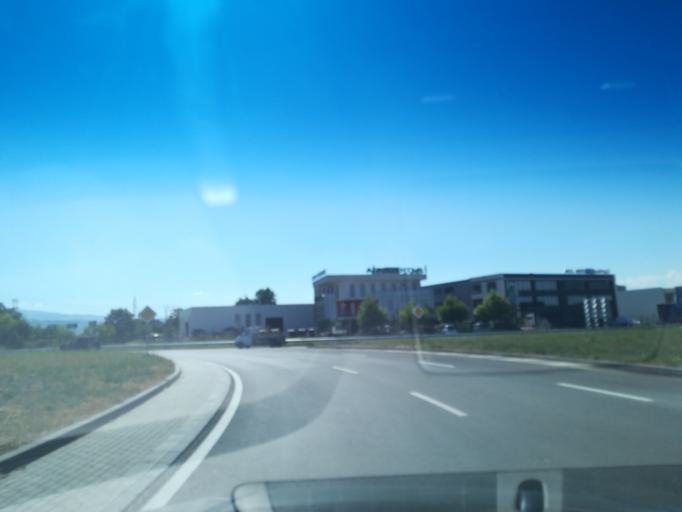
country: BG
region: Plovdiv
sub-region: Obshtina Plovdiv
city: Plovdiv
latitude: 42.0996
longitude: 24.7884
